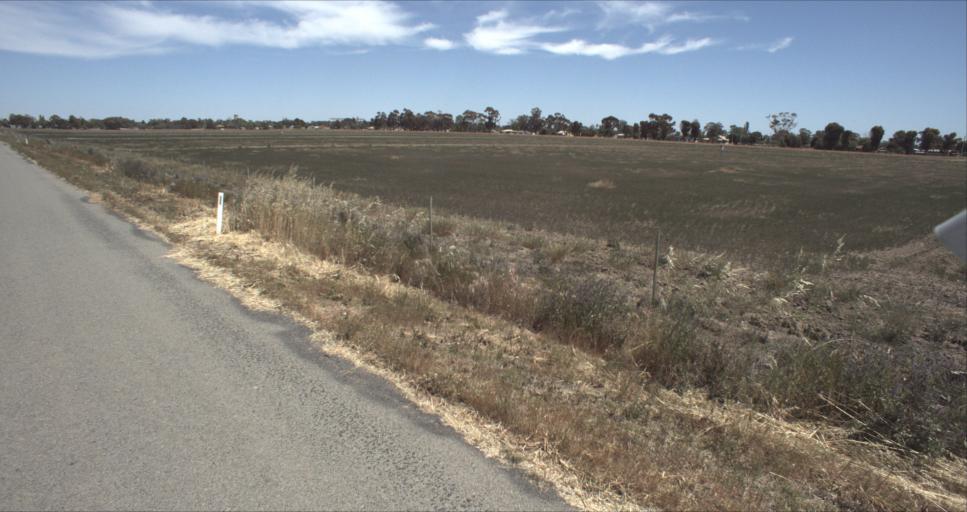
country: AU
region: New South Wales
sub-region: Leeton
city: Leeton
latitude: -34.5938
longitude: 146.4169
